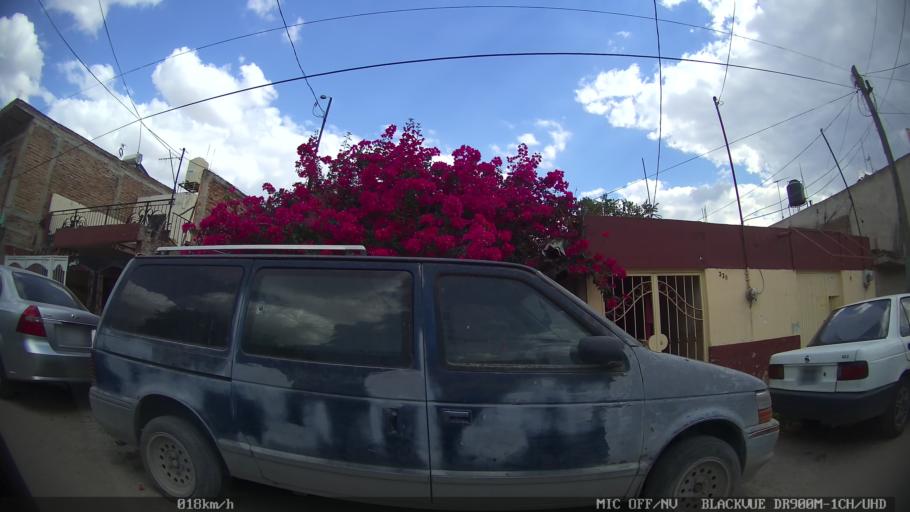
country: MX
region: Jalisco
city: Tonala
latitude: 20.6558
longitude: -103.2535
